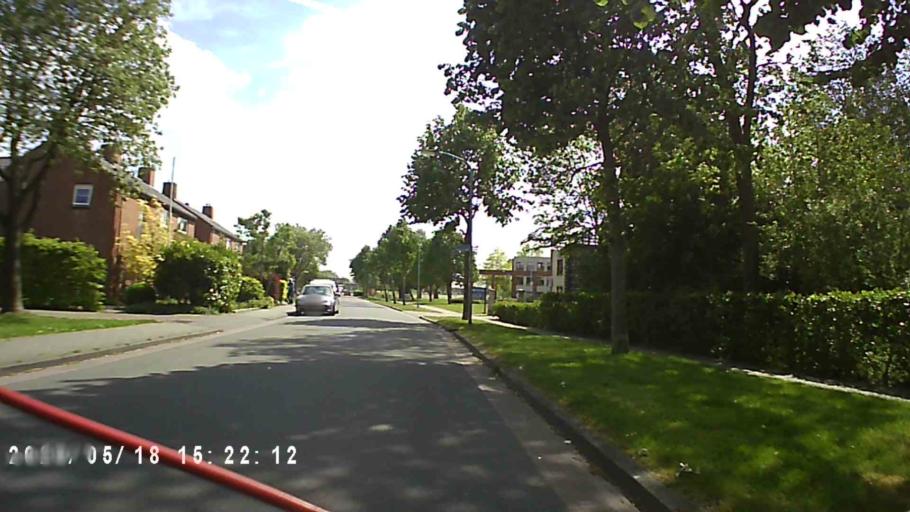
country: NL
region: Groningen
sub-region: Gemeente Winsum
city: Winsum
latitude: 53.3280
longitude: 6.5193
